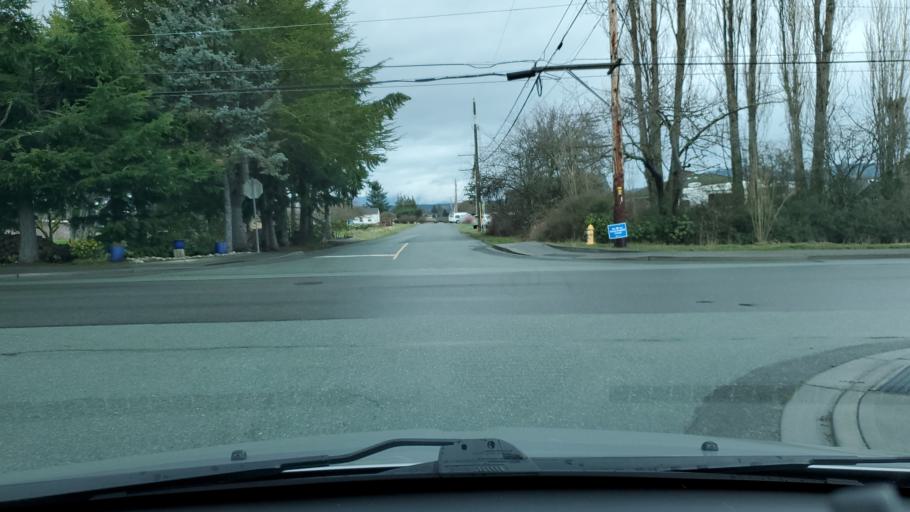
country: US
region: Washington
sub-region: Skagit County
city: Anacortes
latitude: 48.4963
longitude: -122.6206
